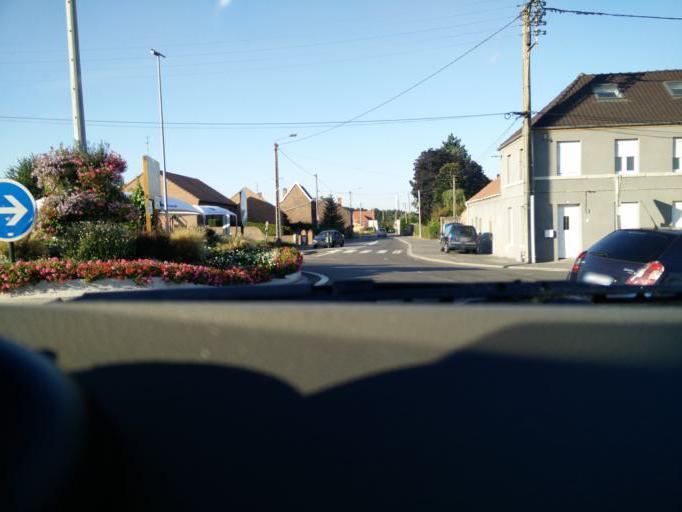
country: FR
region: Nord-Pas-de-Calais
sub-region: Departement du Pas-de-Calais
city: Noyelles-les-Vermelles
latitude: 50.4793
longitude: 2.7350
